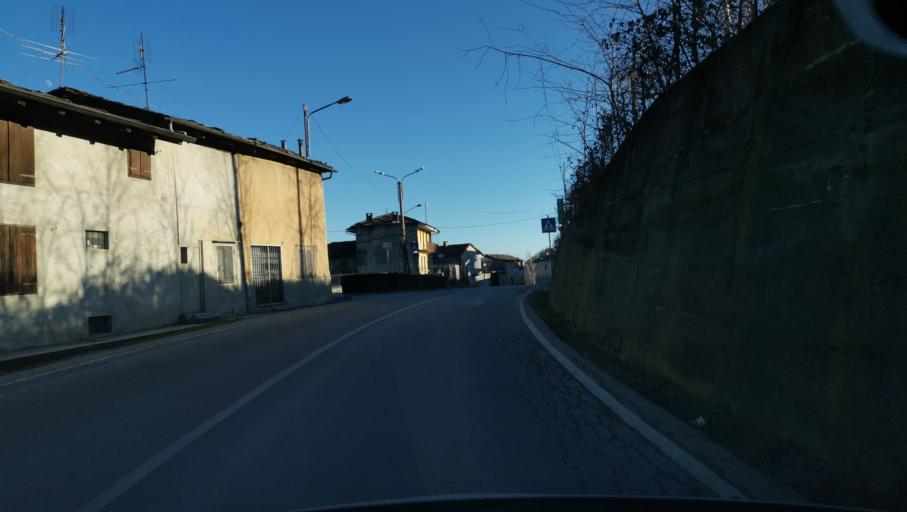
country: IT
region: Piedmont
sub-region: Provincia di Cuneo
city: Bagnolo Piemonte
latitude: 44.7540
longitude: 7.2891
